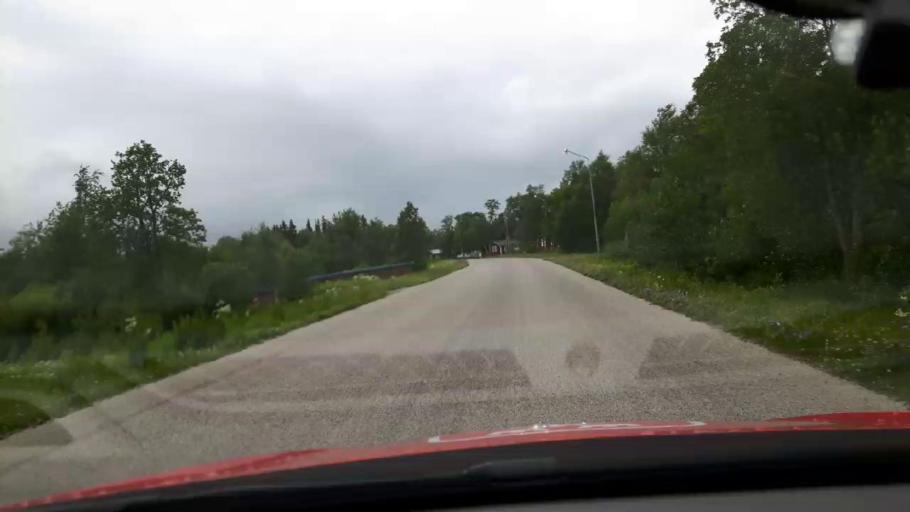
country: SE
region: Jaemtland
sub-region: Are Kommun
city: Are
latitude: 63.2589
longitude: 12.4438
